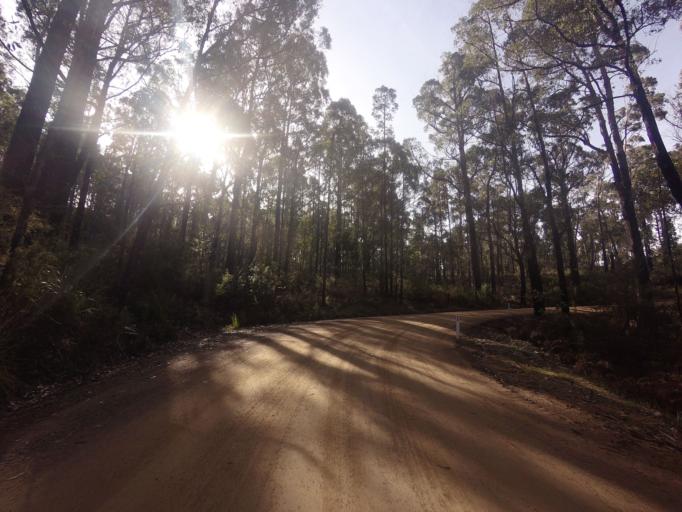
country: AU
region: Tasmania
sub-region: Kingborough
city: Kettering
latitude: -43.0954
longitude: 147.2608
